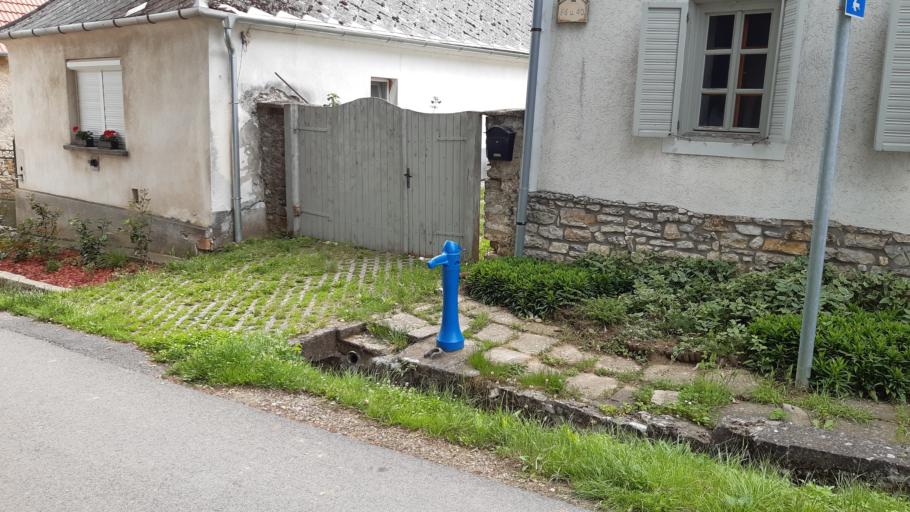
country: HU
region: Veszprem
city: Zanka
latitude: 46.9280
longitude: 17.6685
